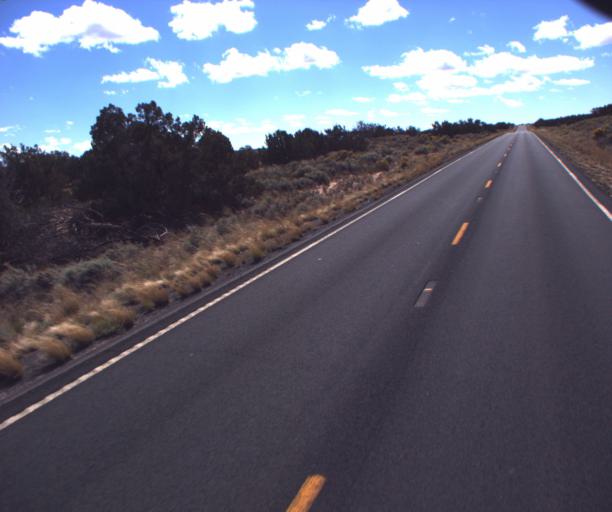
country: US
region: Arizona
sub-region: Apache County
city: Houck
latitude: 35.1515
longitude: -109.3347
